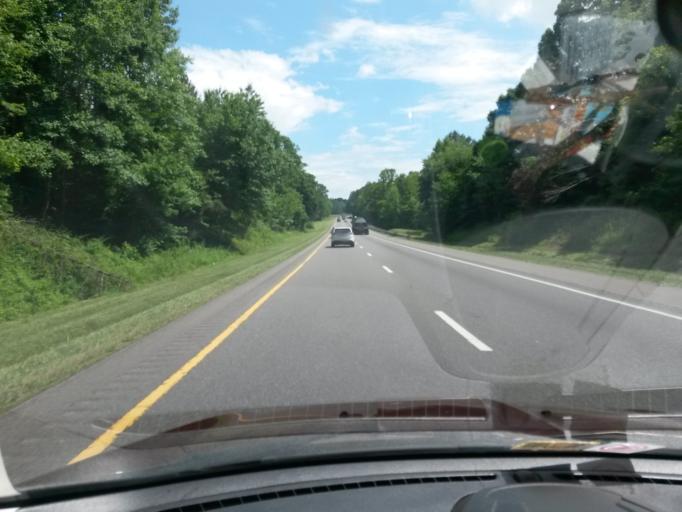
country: US
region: North Carolina
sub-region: Surry County
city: Dobson
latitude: 36.4344
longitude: -80.7781
